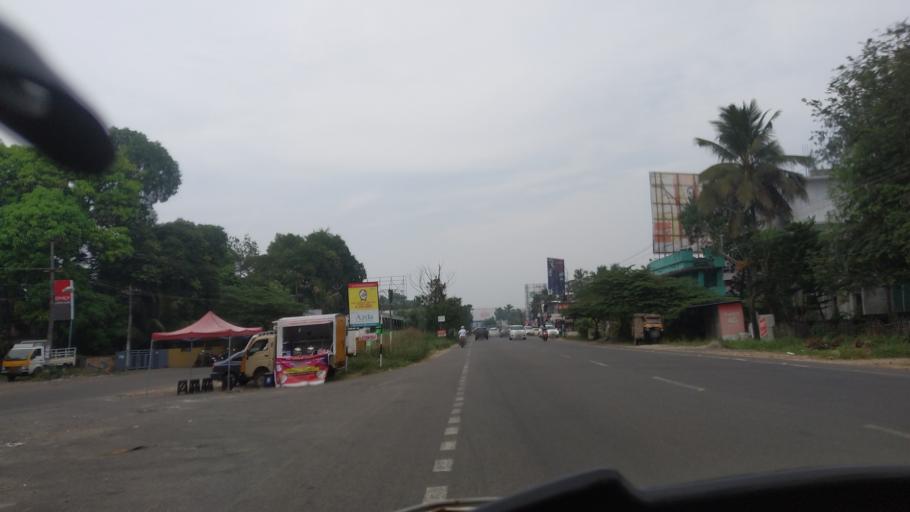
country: IN
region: Kerala
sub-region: Ernakulam
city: Elur
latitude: 10.0540
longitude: 76.2926
